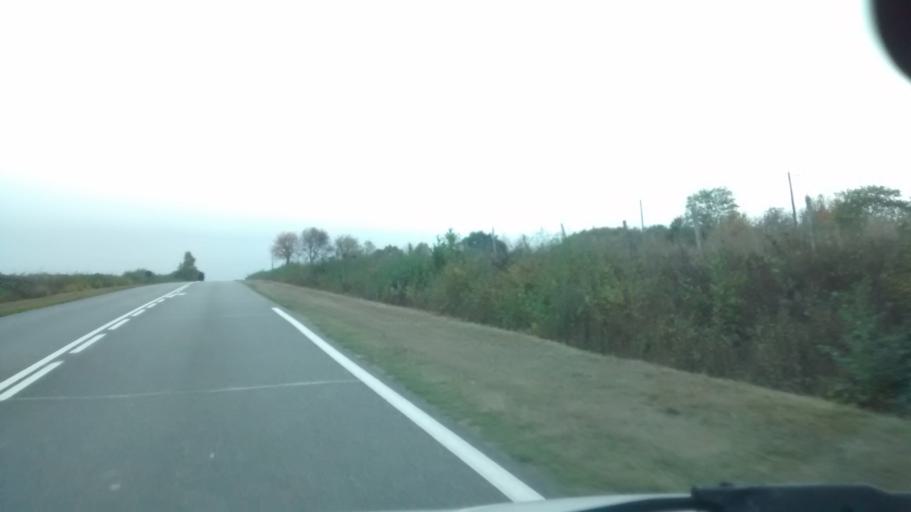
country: FR
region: Brittany
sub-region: Departement d'Ille-et-Vilaine
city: Acigne
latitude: 48.1548
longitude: -1.5173
